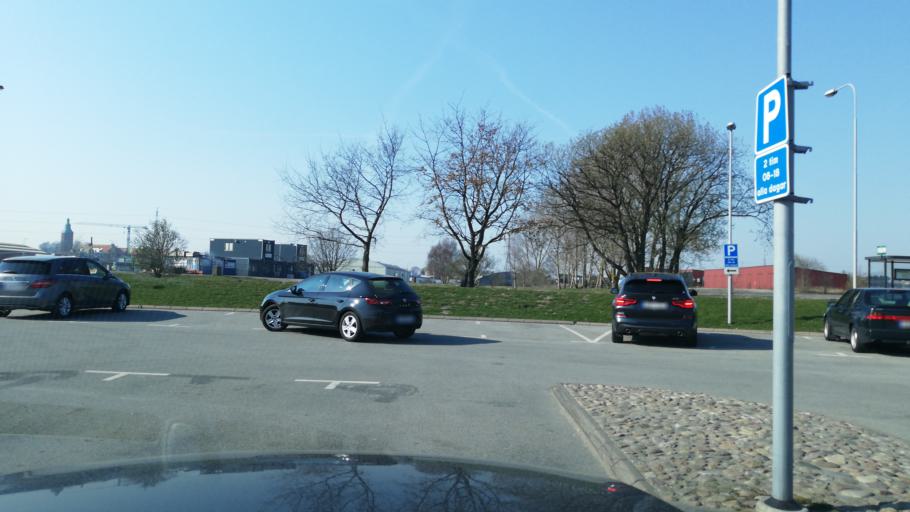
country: SE
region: Skane
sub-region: Ystads Kommun
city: Ystad
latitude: 55.4340
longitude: 13.8410
